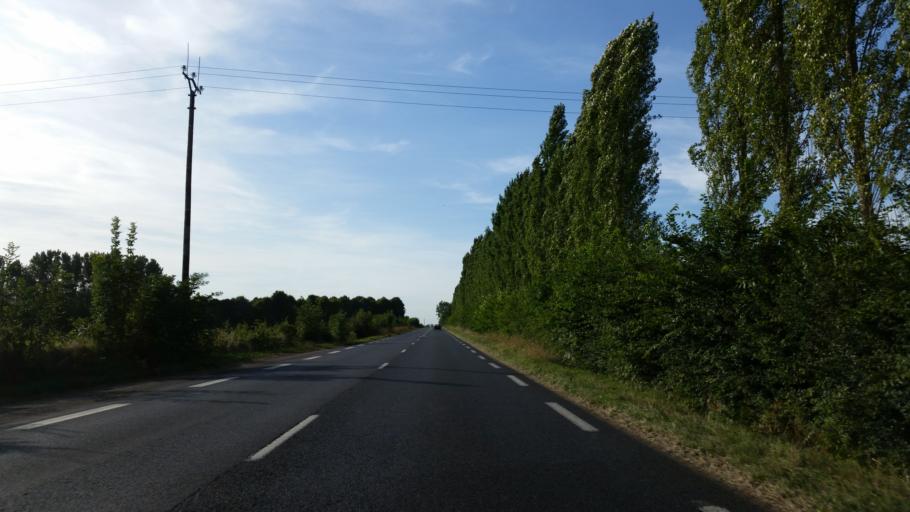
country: FR
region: Lower Normandy
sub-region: Departement du Calvados
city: Cambremer
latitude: 49.1236
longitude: 0.0096
